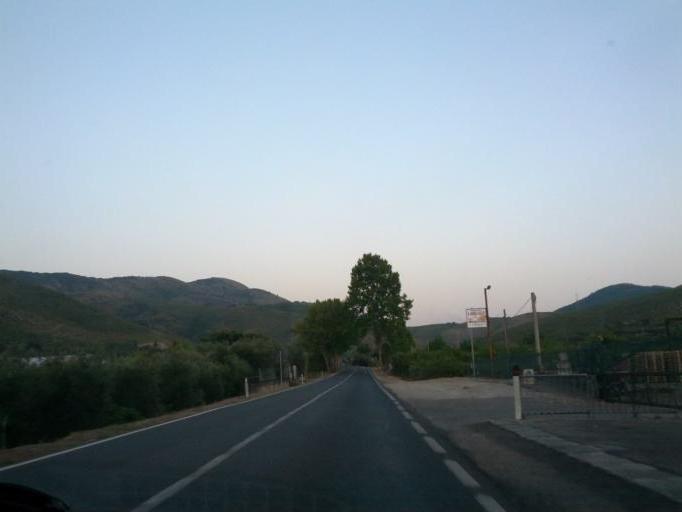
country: IT
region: Latium
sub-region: Provincia di Latina
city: Fondi
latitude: 41.3309
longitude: 13.4664
